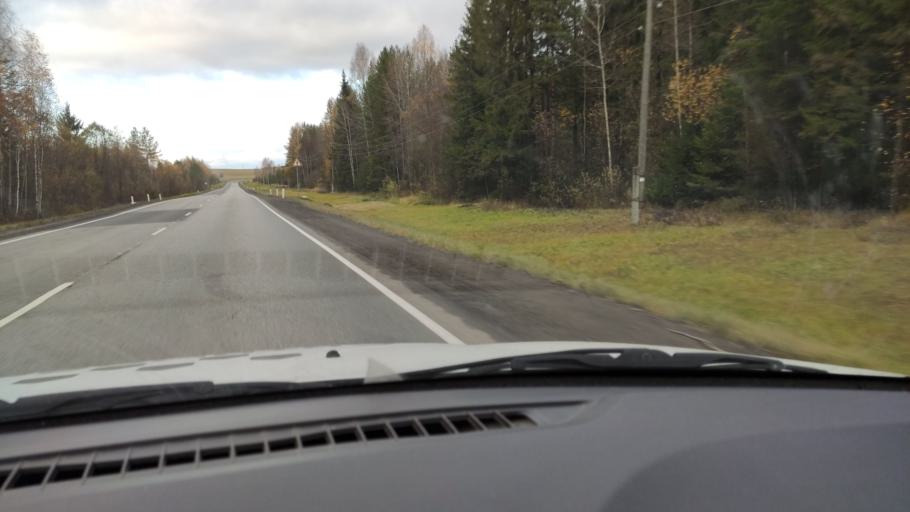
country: RU
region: Kirov
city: Belaya Kholunitsa
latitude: 58.8847
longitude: 50.8734
